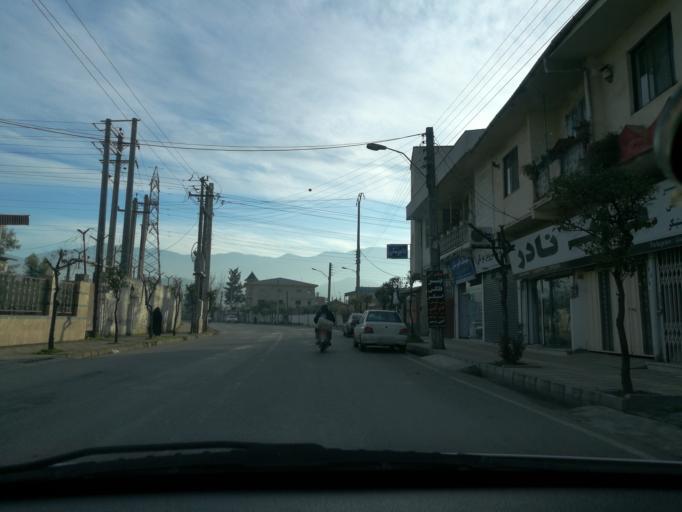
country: IR
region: Mazandaran
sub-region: Nowshahr
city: Nowshahr
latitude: 36.6395
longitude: 51.5025
